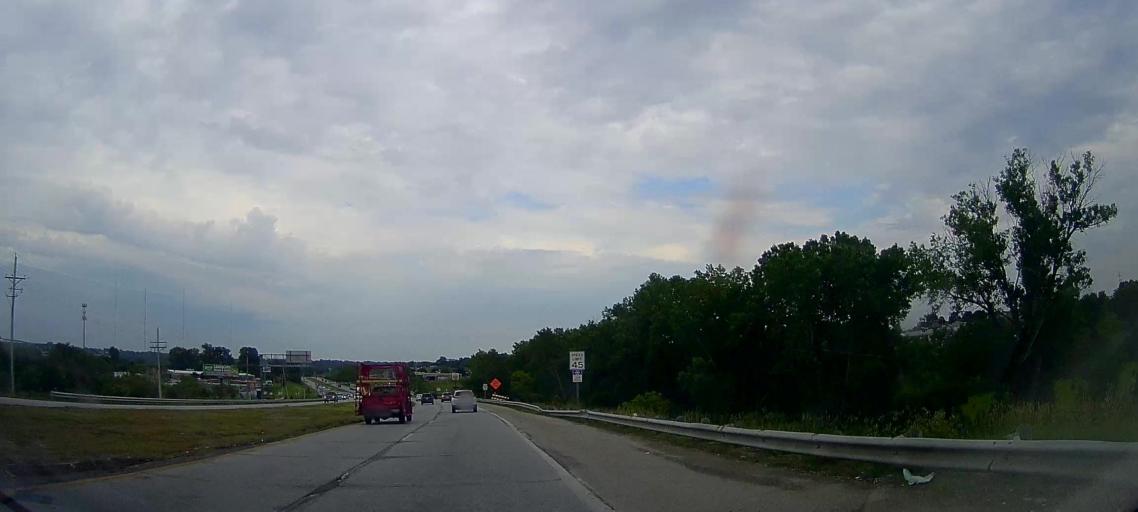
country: US
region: Nebraska
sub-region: Douglas County
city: Bennington
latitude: 41.3209
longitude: -96.0678
